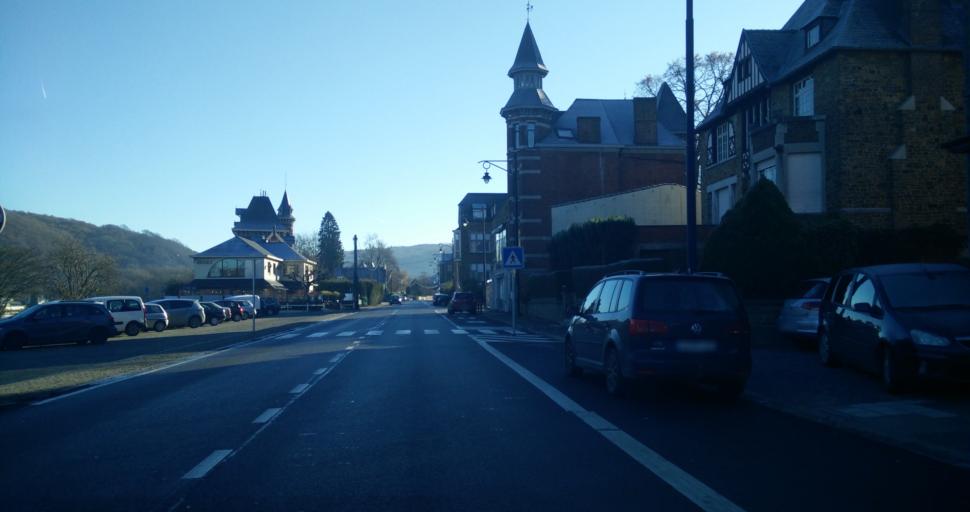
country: BE
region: Wallonia
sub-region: Province de Namur
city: Namur
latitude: 50.4240
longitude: 4.8730
